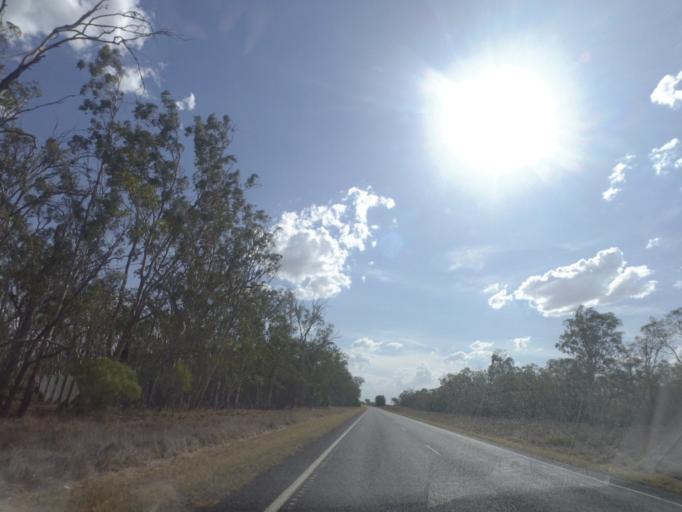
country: AU
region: New South Wales
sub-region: Moree Plains
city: Boggabilla
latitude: -28.5473
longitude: 150.8739
